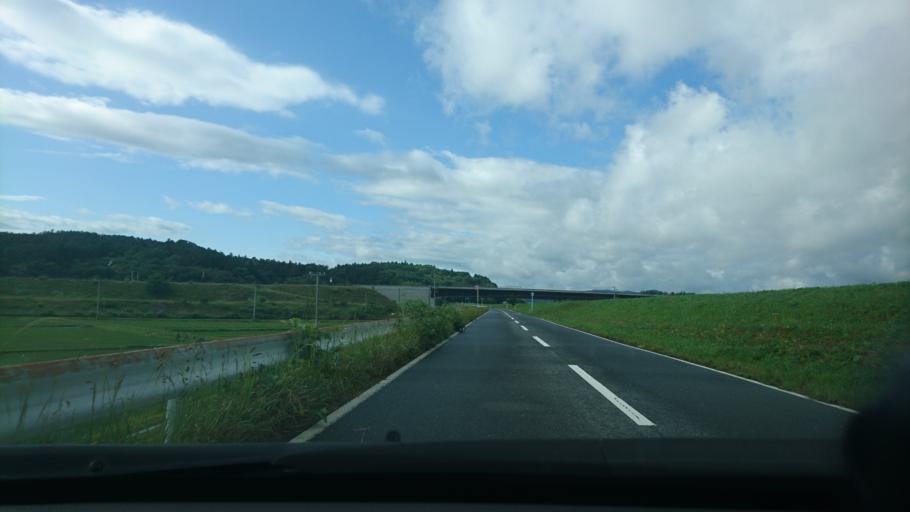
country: JP
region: Miyagi
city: Wakuya
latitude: 38.6953
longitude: 141.2851
